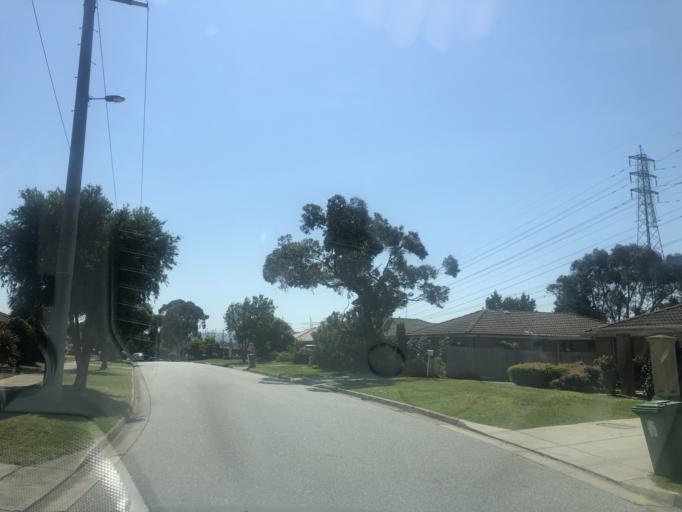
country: AU
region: Victoria
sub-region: Casey
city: Narre Warren South
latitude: -38.0440
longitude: 145.2822
